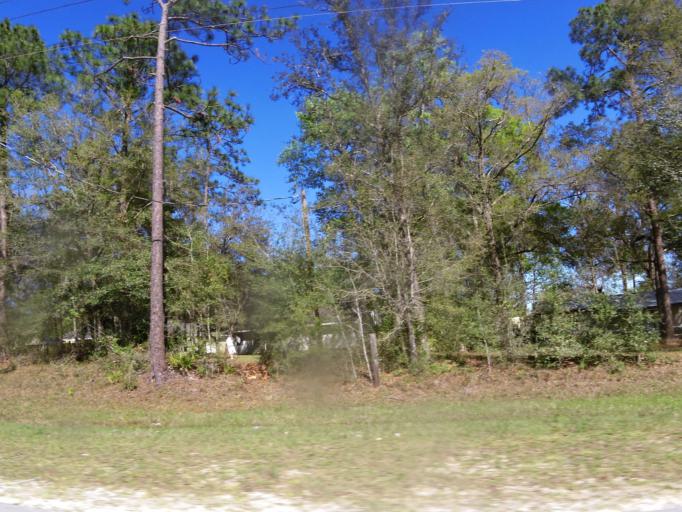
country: US
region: Florida
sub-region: Clay County
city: Keystone Heights
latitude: 29.8209
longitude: -82.0580
